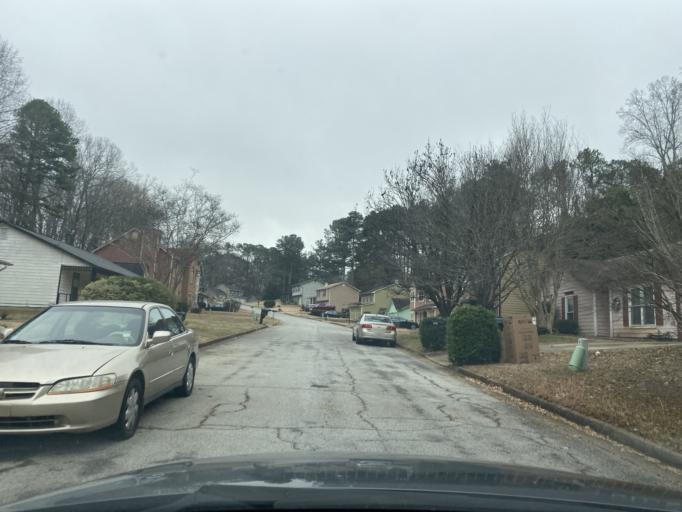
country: US
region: Georgia
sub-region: DeKalb County
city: Pine Mountain
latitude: 33.6884
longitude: -84.1651
